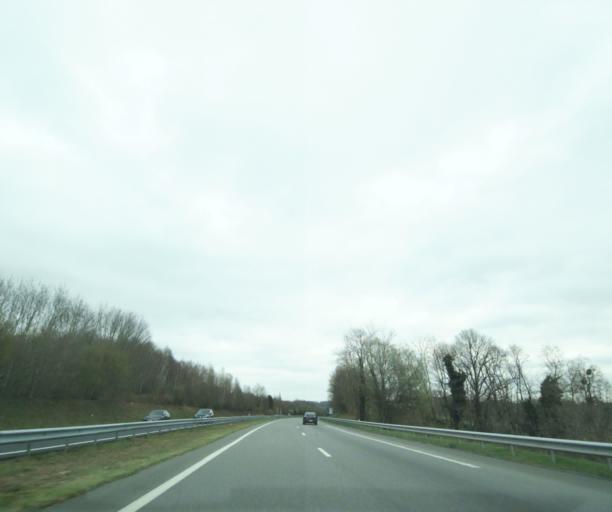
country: FR
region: Limousin
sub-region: Departement de la Correze
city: Uzerche
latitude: 45.3894
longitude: 1.5735
